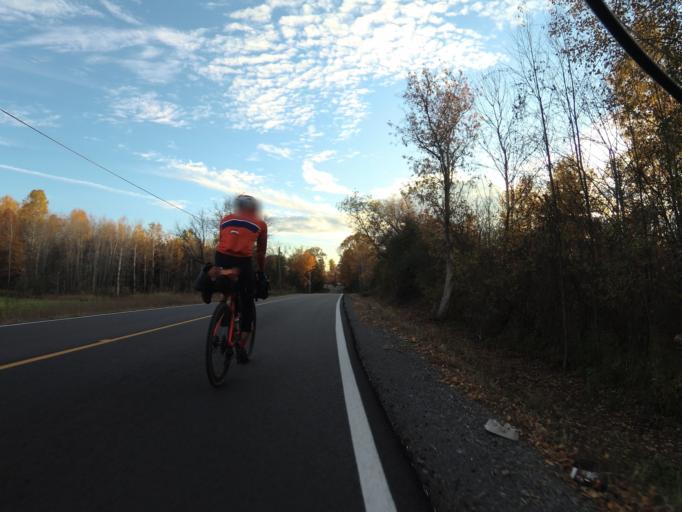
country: CA
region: Ontario
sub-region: Lanark County
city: Smiths Falls
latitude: 44.9469
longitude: -75.8183
